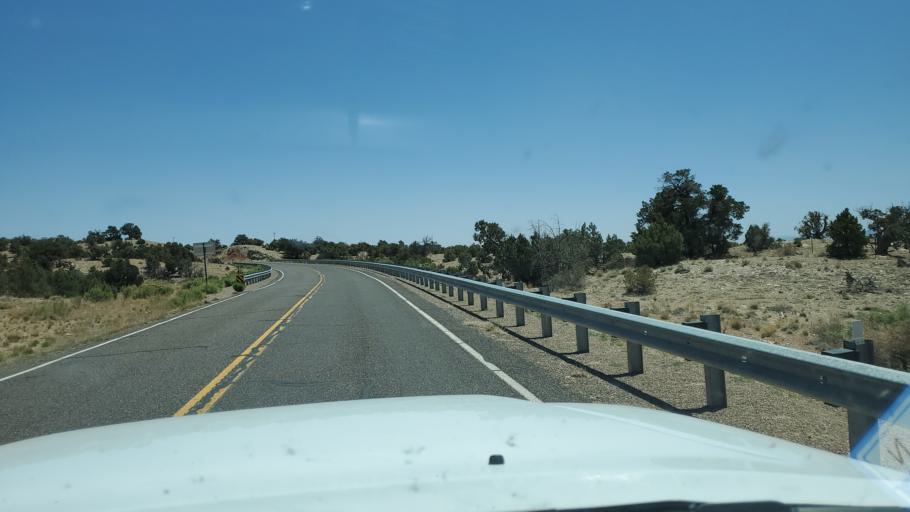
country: US
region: Utah
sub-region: Wayne County
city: Loa
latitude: 37.7271
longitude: -111.5287
